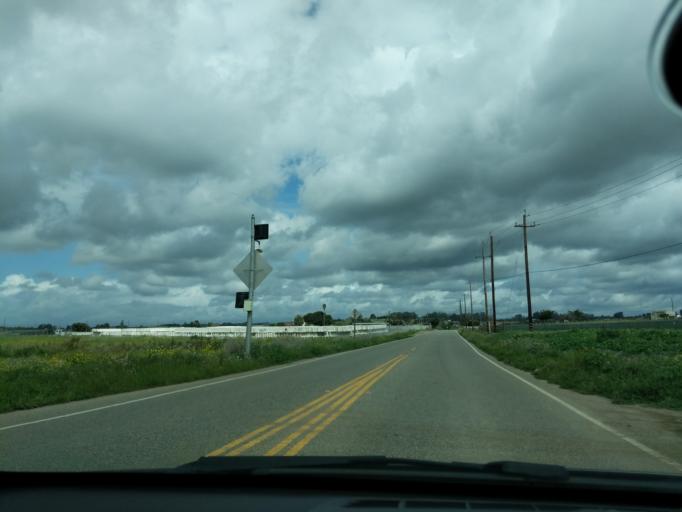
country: US
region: California
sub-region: Monterey County
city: Prunedale
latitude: 36.7457
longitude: -121.6572
